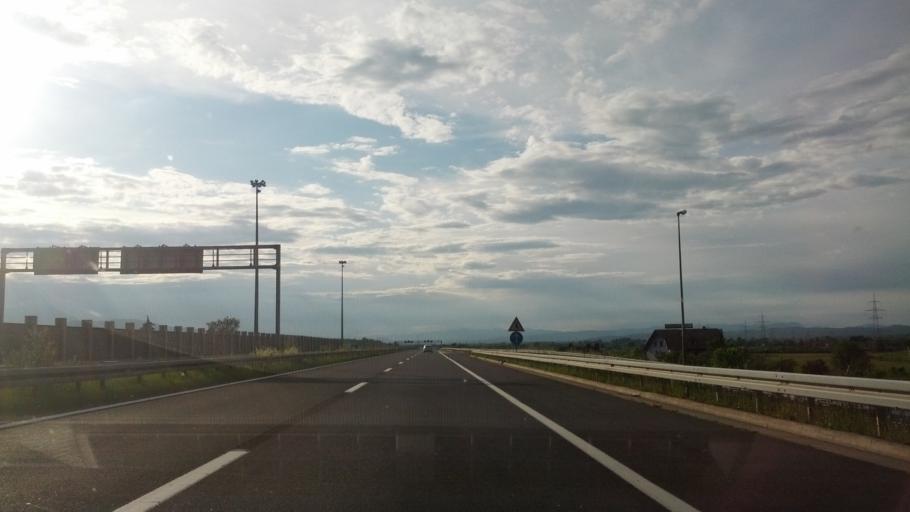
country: HR
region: Zagrebacka
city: Bestovje
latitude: 45.7990
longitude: 15.7837
